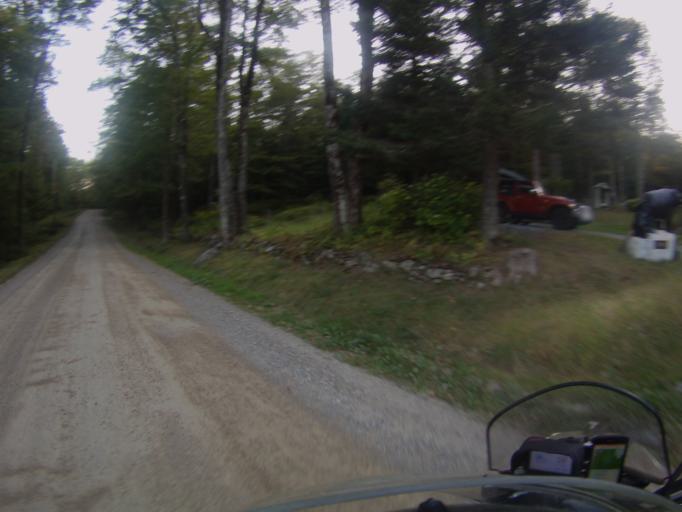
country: US
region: Vermont
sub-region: Addison County
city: Bristol
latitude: 44.0144
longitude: -73.0280
